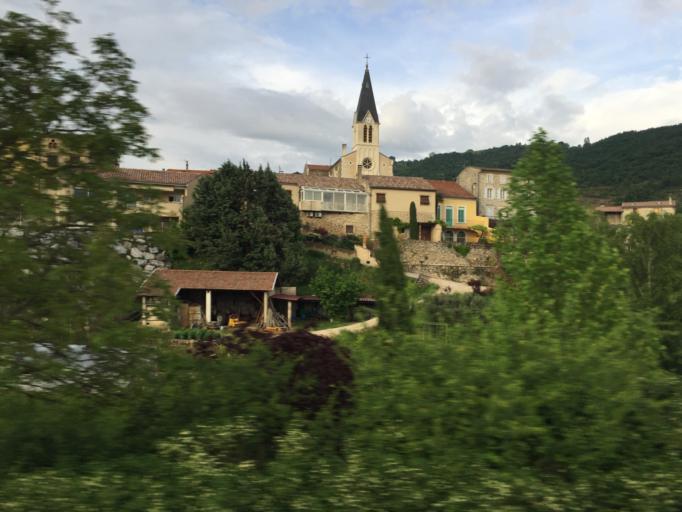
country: FR
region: Rhone-Alpes
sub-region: Departement de l'Ardeche
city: Saint-Jean-de-Muzols
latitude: 45.1069
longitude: 4.8308
